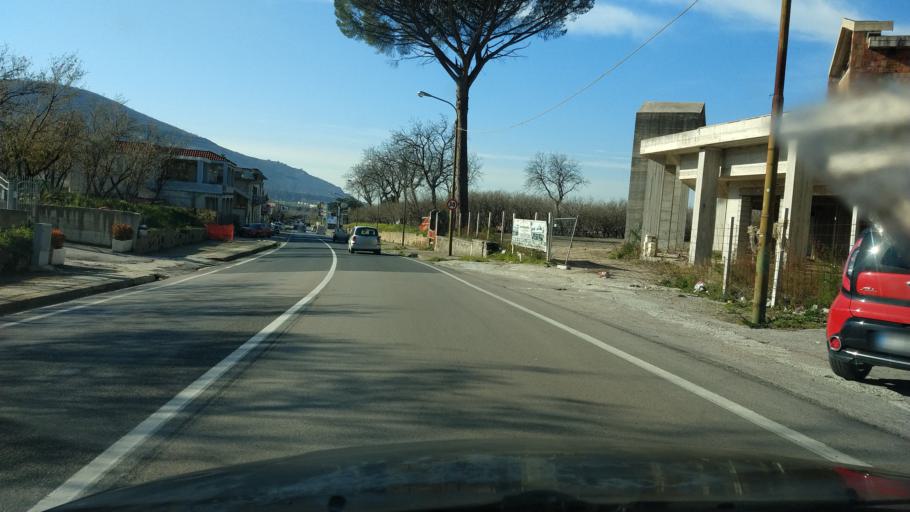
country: IT
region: Campania
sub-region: Provincia di Avellino
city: Avella
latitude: 40.9522
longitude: 14.5908
